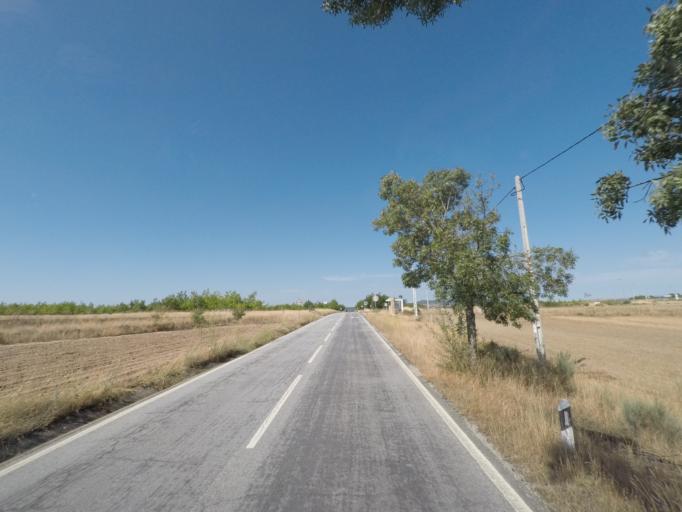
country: ES
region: Castille and Leon
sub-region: Provincia de Salamanca
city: Villarino de los Aires
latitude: 41.3664
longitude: -6.5037
